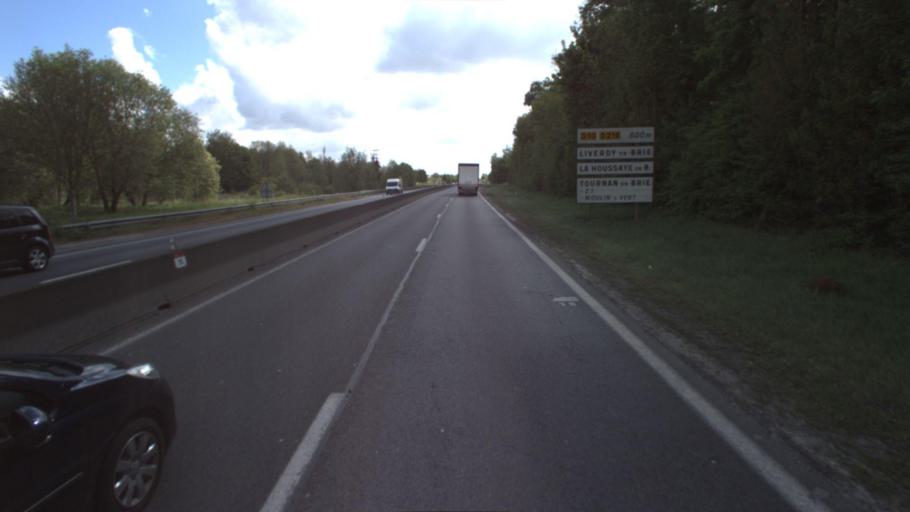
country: FR
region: Ile-de-France
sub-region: Departement de Seine-et-Marne
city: Tournan-en-Brie
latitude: 48.7365
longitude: 2.7668
